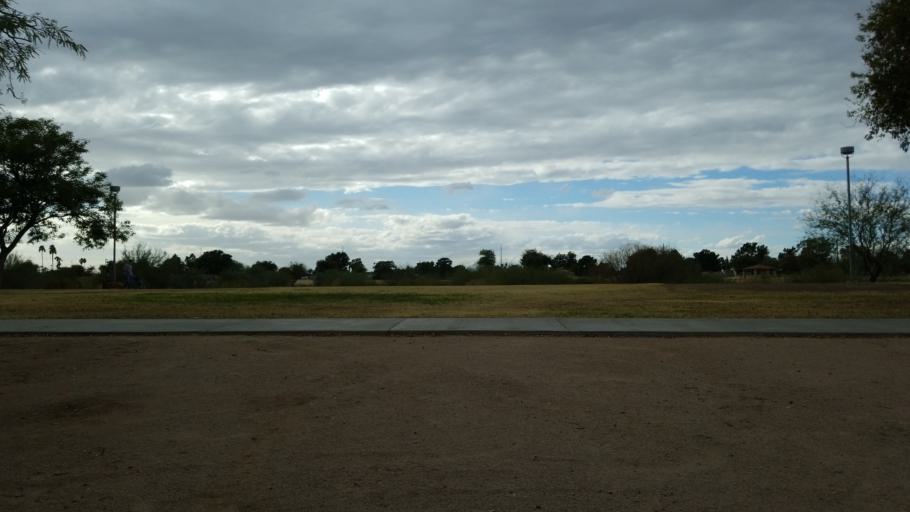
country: US
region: Arizona
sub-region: Maricopa County
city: Glendale
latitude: 33.6064
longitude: -112.1088
